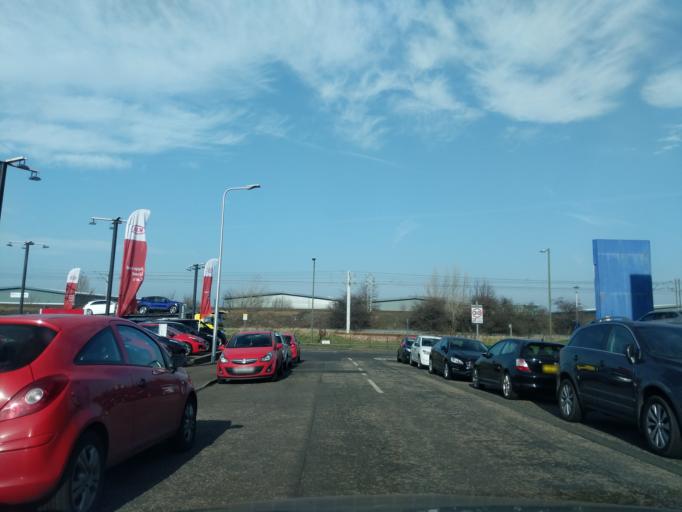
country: GB
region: Scotland
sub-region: Edinburgh
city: Currie
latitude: 55.9276
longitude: -3.2987
